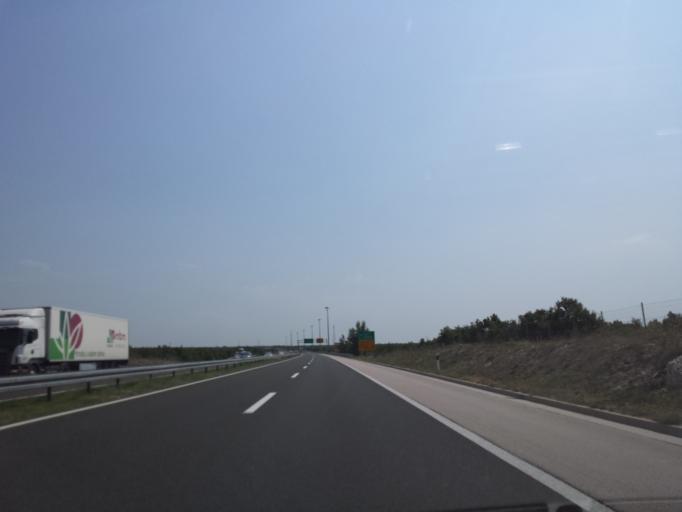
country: HR
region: Zadarska
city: Benkovac
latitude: 44.0163
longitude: 15.5779
